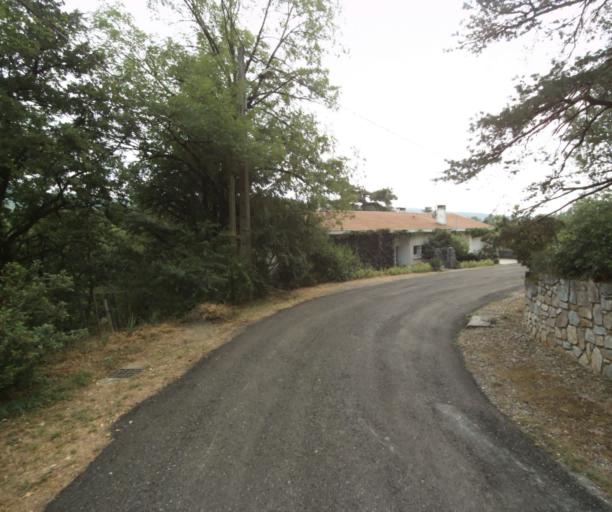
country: FR
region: Midi-Pyrenees
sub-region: Departement de la Haute-Garonne
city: Revel
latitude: 43.4367
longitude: 2.0156
